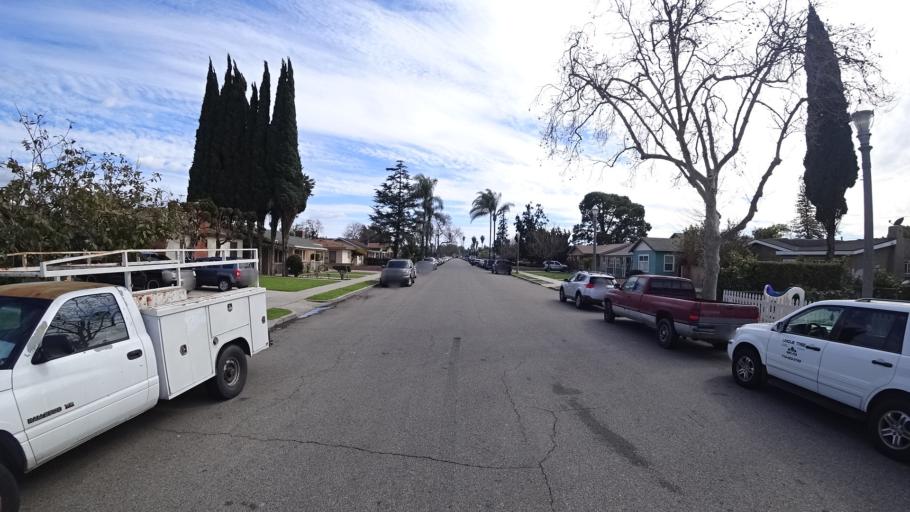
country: US
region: California
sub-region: Orange County
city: Anaheim
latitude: 33.8442
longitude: -117.9141
